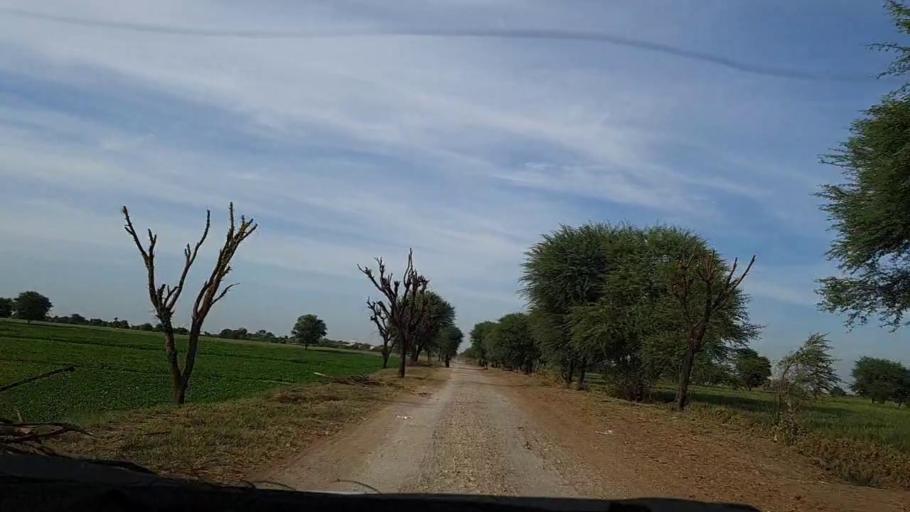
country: PK
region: Sindh
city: Dhoro Naro
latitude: 25.4432
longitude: 69.5123
